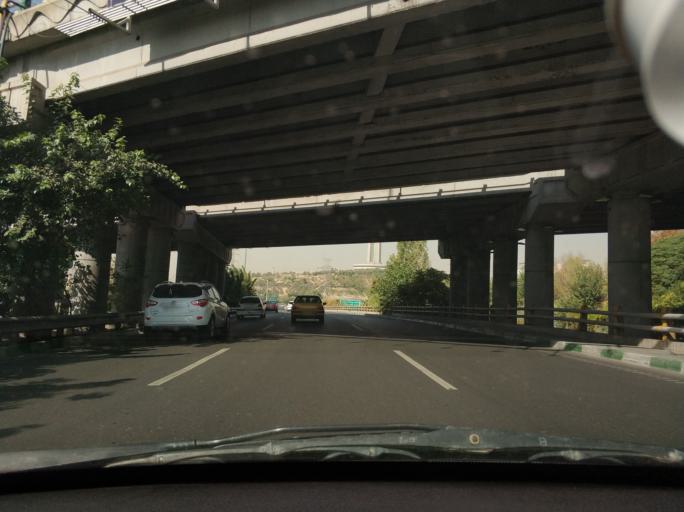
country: IR
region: Tehran
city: Tehran
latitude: 35.7436
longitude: 51.3873
